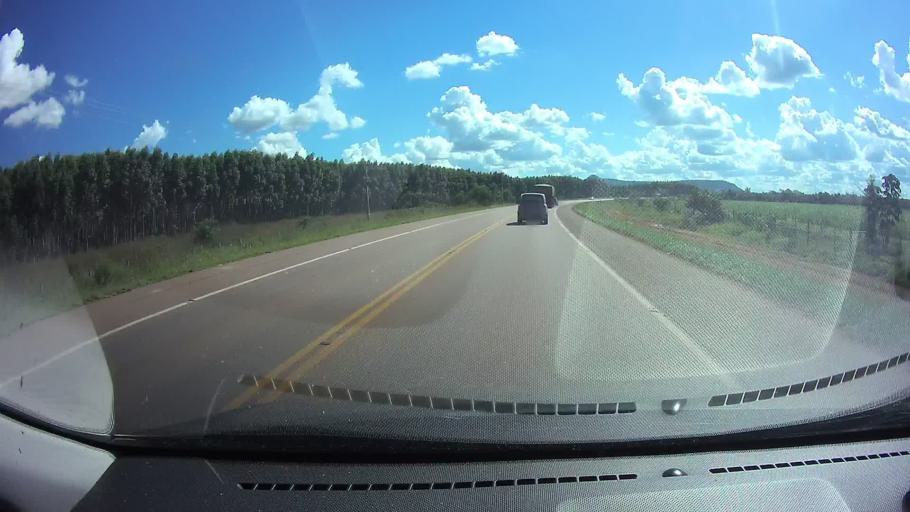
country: PY
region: Guaira
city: Coronel Martinez
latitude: -25.7634
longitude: -56.7237
